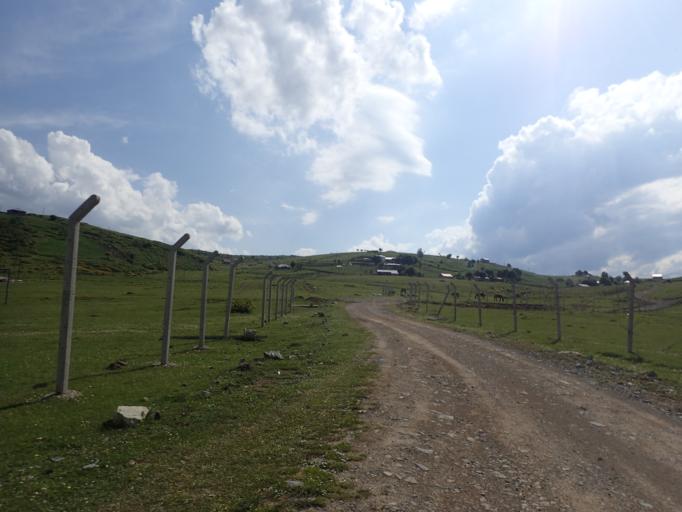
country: TR
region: Ordu
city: Topcam
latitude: 40.6816
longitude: 37.9217
